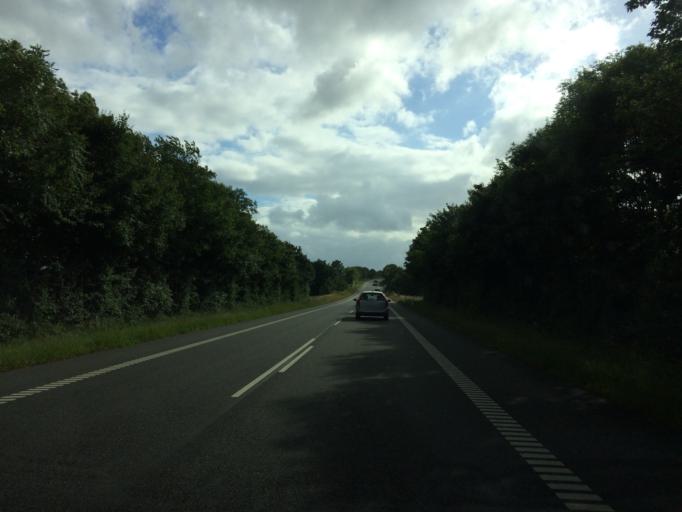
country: DK
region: South Denmark
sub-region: Sonderborg Kommune
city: Guderup
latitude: 54.9764
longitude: 9.9564
